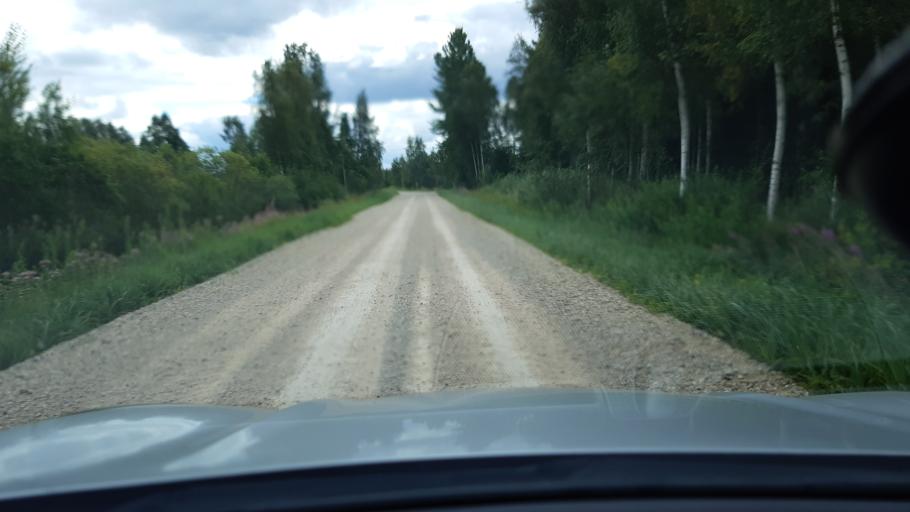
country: EE
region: Raplamaa
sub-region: Jaervakandi vald
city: Jarvakandi
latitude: 58.8016
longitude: 24.8573
